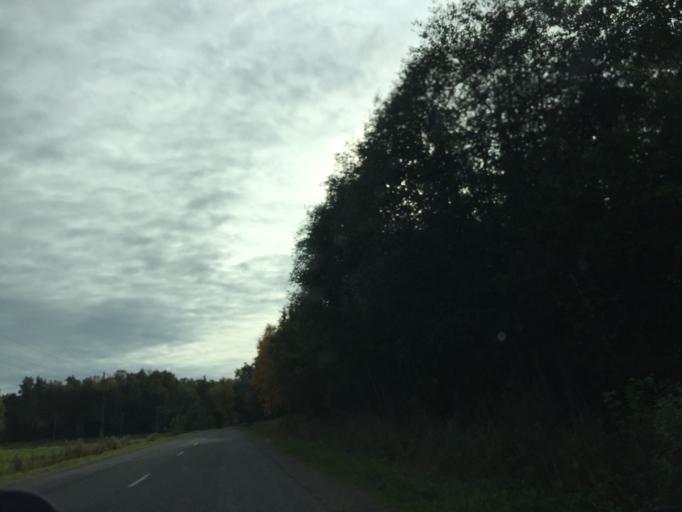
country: LV
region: Auces Novads
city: Auce
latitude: 56.5557
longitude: 23.0181
